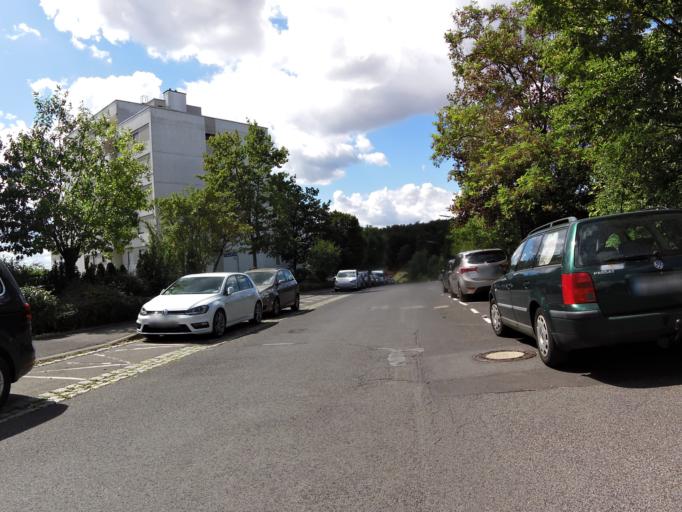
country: DE
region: Bavaria
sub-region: Regierungsbezirk Unterfranken
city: Hochberg
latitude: 49.7910
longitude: 9.8847
